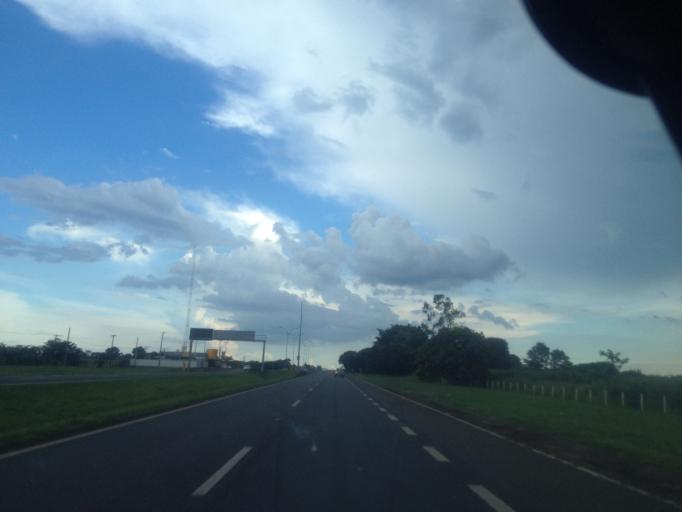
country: BR
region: Sao Paulo
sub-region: Pirassununga
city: Pirassununga
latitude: -22.0159
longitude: -47.4399
